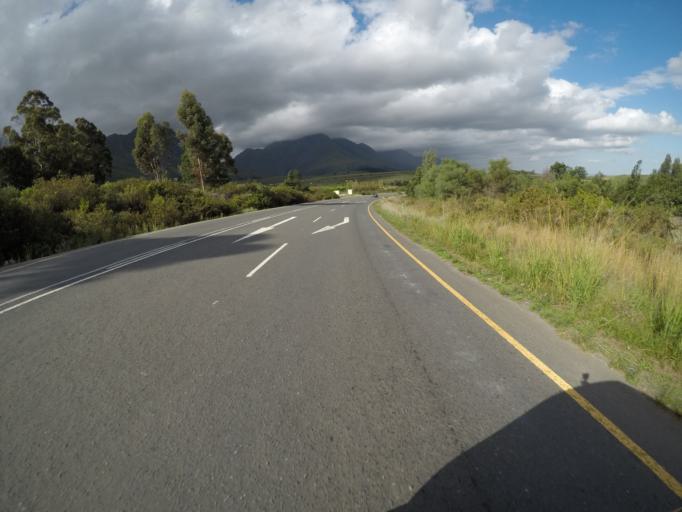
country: ZA
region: Western Cape
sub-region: Overberg District Municipality
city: Swellendam
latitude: -33.9938
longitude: 20.3488
